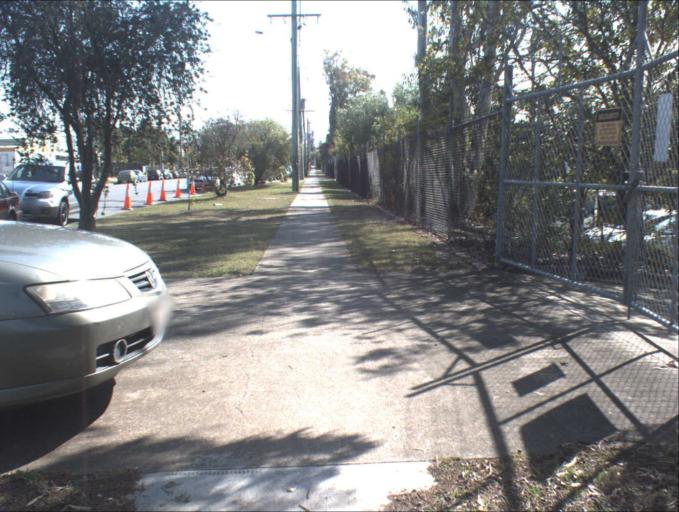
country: AU
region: Queensland
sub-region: Logan
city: Logan Reserve
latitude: -27.6860
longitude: 153.0778
